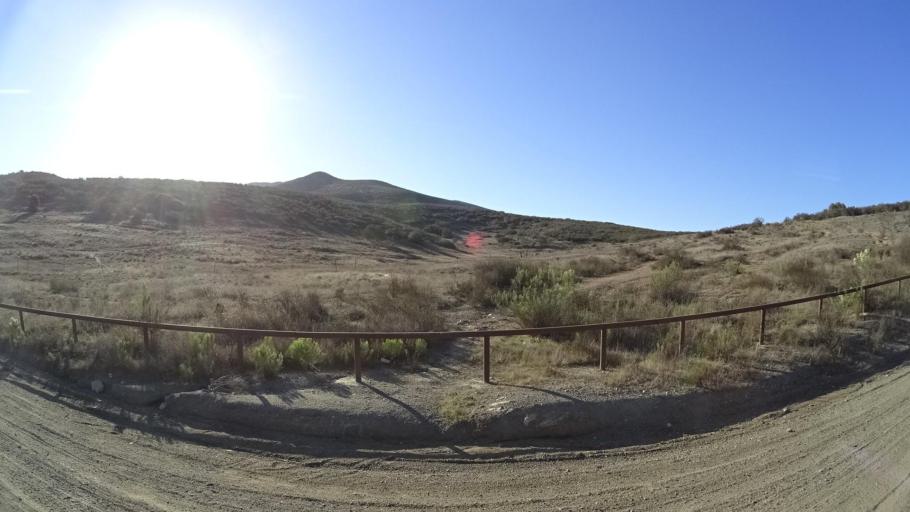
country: US
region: California
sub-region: San Diego County
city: Jamul
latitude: 32.6926
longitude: -116.9033
